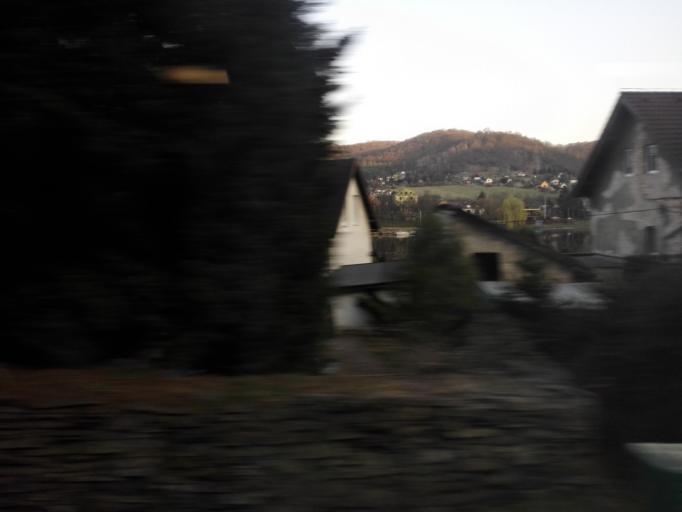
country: CZ
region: Ustecky
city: Trmice
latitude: 50.5921
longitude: 14.0323
